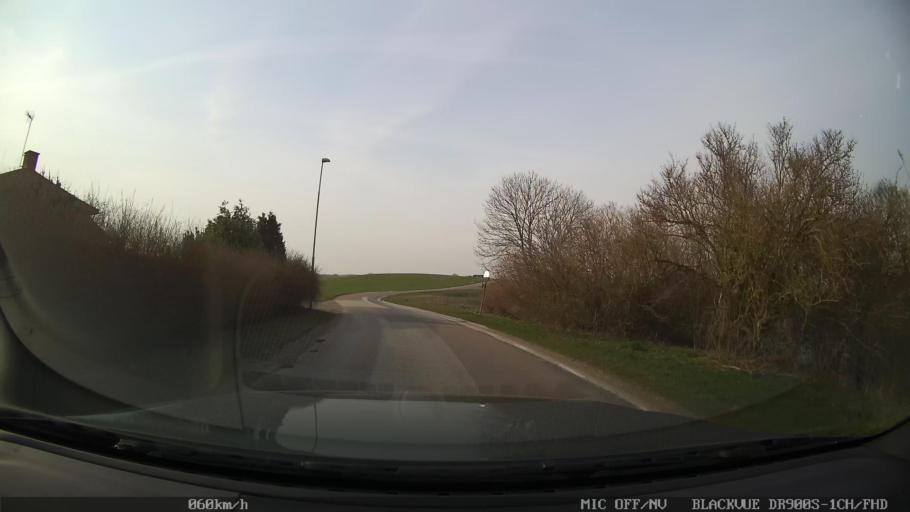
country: SE
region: Skane
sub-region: Ystads Kommun
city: Ystad
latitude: 55.4476
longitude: 13.8327
